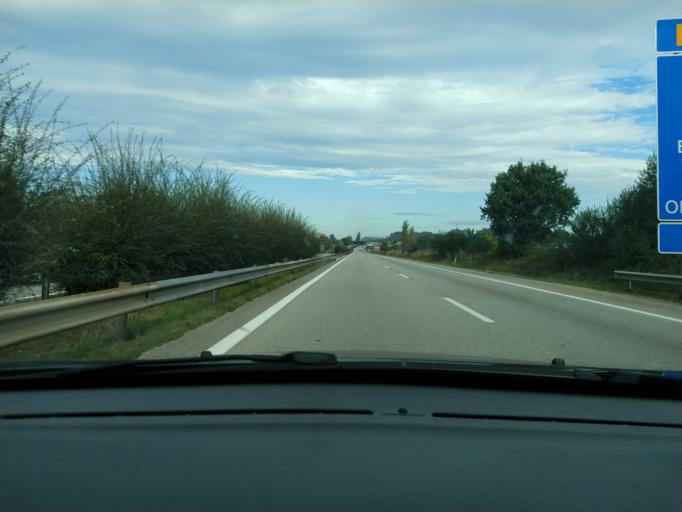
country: PT
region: Aveiro
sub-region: Estarreja
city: Beduido
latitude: 40.7609
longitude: -8.5395
